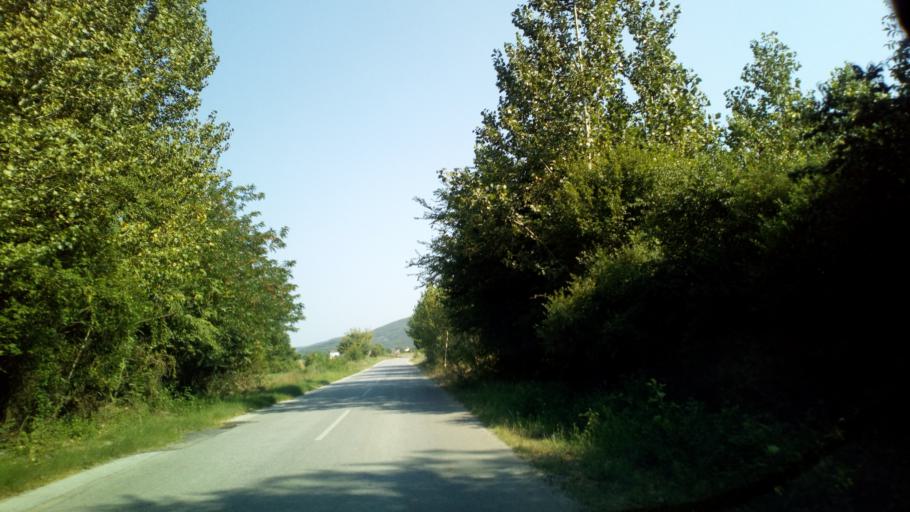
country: GR
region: Central Macedonia
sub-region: Nomos Chalkidikis
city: Galatista
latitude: 40.5647
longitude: 23.2917
